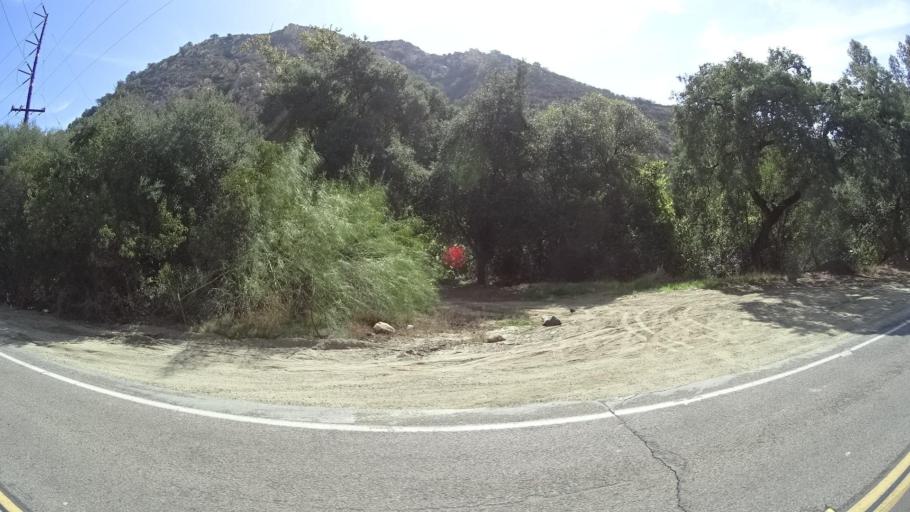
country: US
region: California
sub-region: San Diego County
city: Harbison Canyon
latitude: 32.8265
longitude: -116.8244
